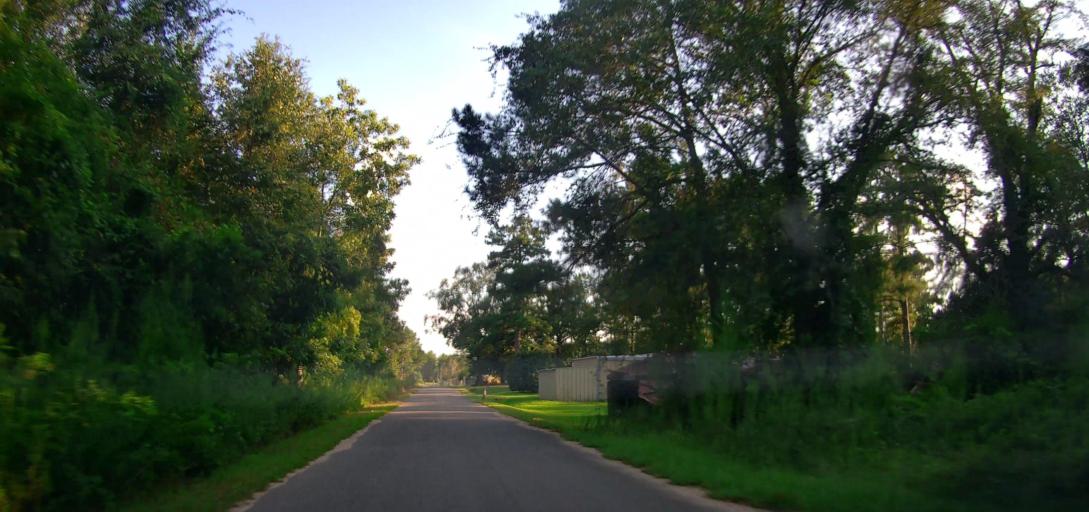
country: US
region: Georgia
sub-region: Crawford County
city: Roberta
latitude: 32.7058
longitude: -84.0088
